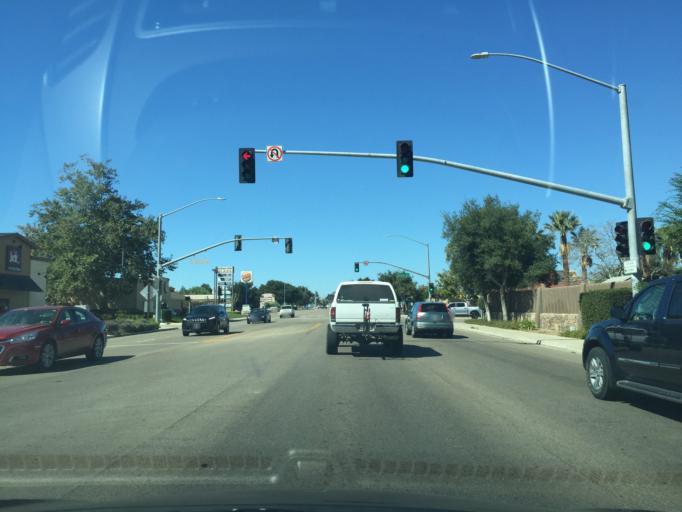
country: US
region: California
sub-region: Santa Barbara County
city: Buellton
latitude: 34.6104
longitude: -120.1857
